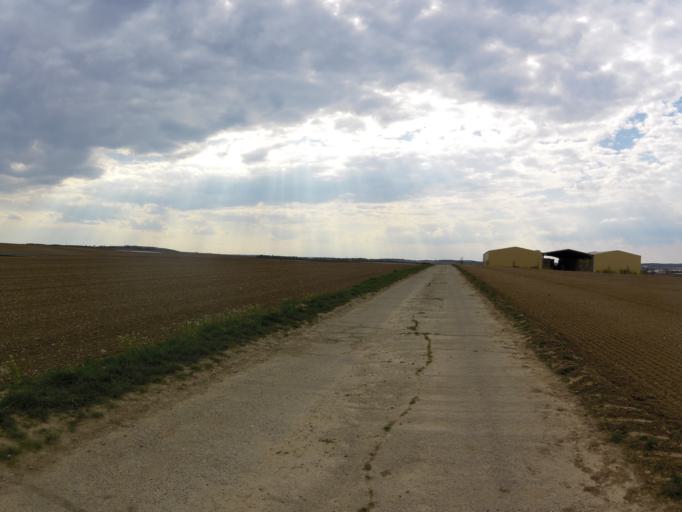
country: DE
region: Bavaria
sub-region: Regierungsbezirk Unterfranken
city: Oberpleichfeld
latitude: 49.8643
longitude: 10.0907
